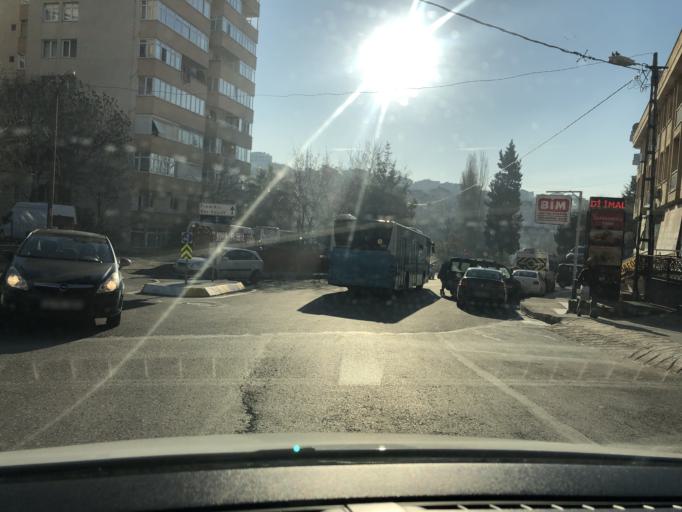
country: TR
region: Istanbul
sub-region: Atasehir
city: Atasehir
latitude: 40.9683
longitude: 29.1195
